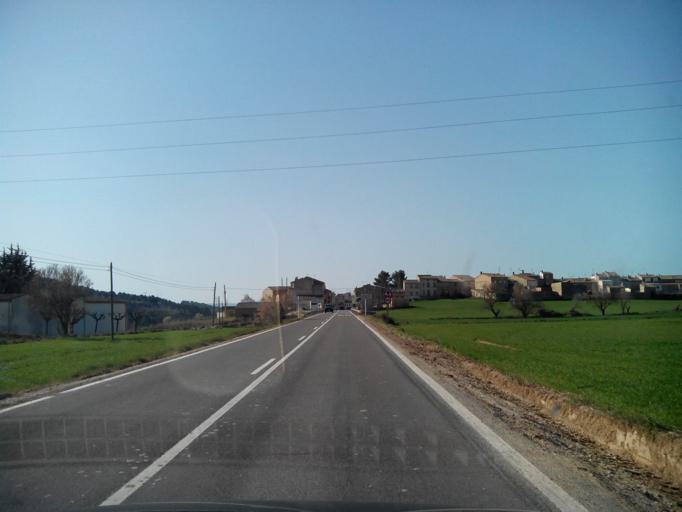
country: ES
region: Catalonia
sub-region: Provincia de Tarragona
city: Conesa
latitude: 41.4788
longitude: 1.2856
